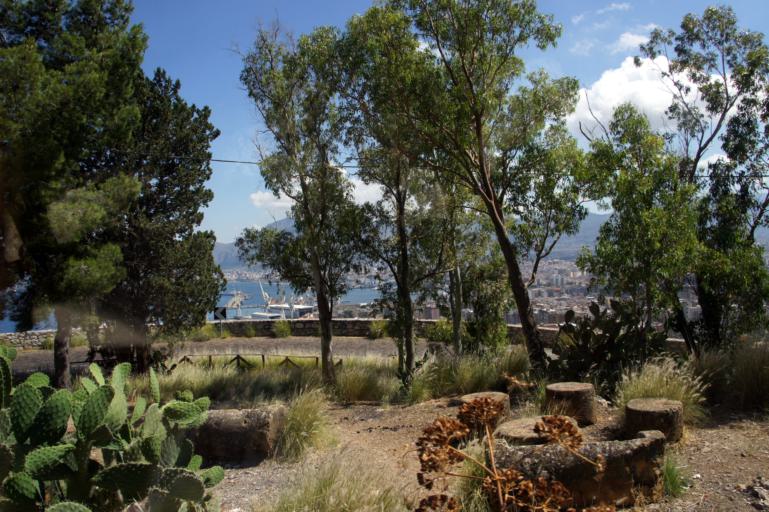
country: IT
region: Sicily
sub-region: Palermo
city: Palermo
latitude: 38.1543
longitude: 13.3597
